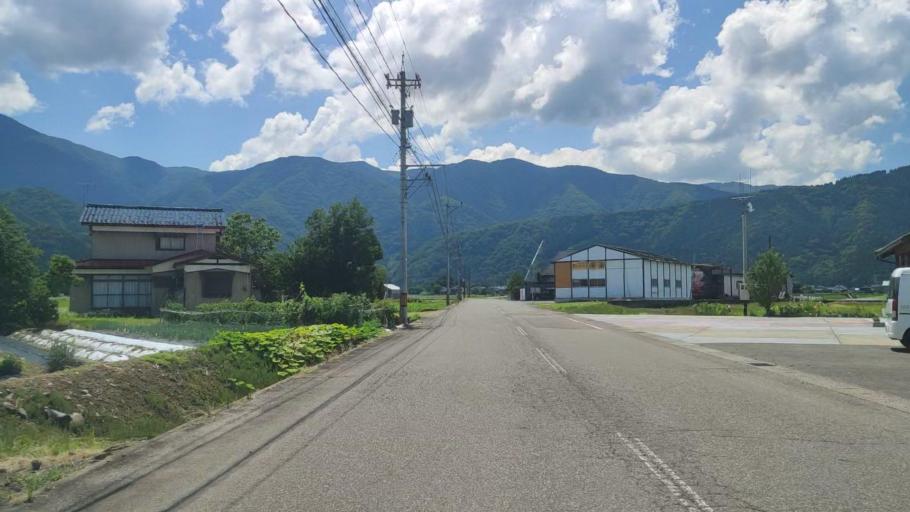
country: JP
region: Fukui
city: Ono
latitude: 35.9484
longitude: 136.5415
